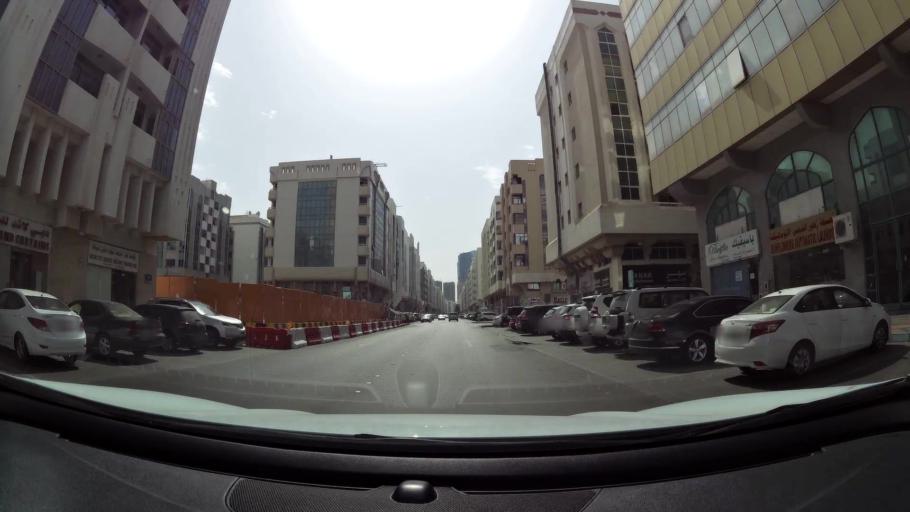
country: AE
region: Abu Dhabi
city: Abu Dhabi
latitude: 24.4796
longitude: 54.3585
